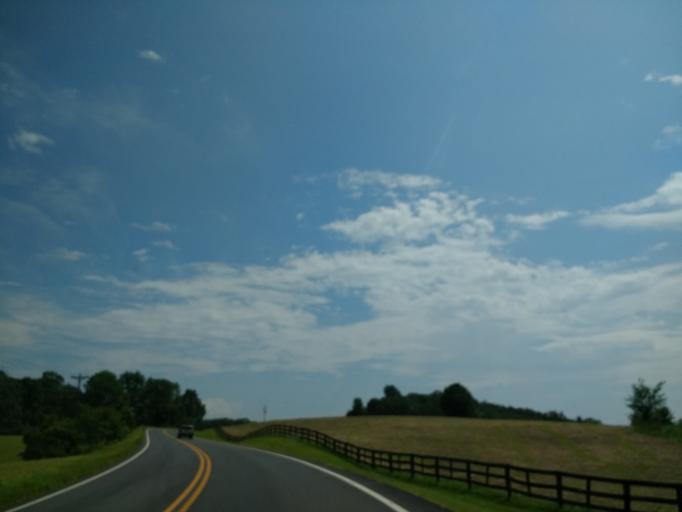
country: US
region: Georgia
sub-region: White County
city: Cleveland
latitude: 34.6544
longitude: -83.7960
